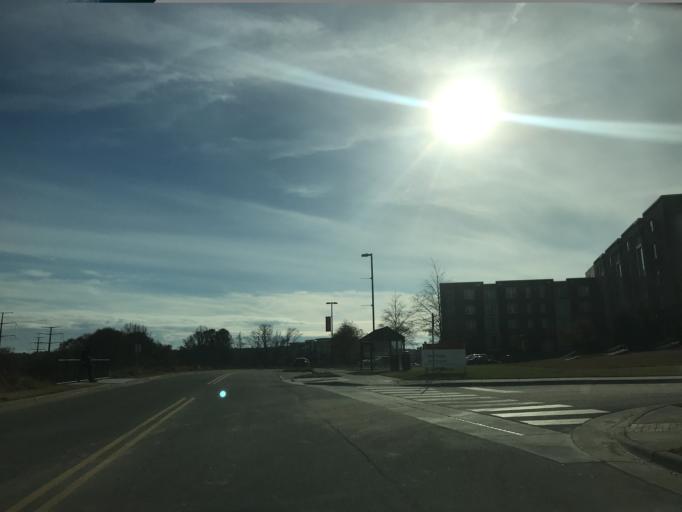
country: US
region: North Carolina
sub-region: Wake County
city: West Raleigh
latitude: 35.7695
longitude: -78.6719
